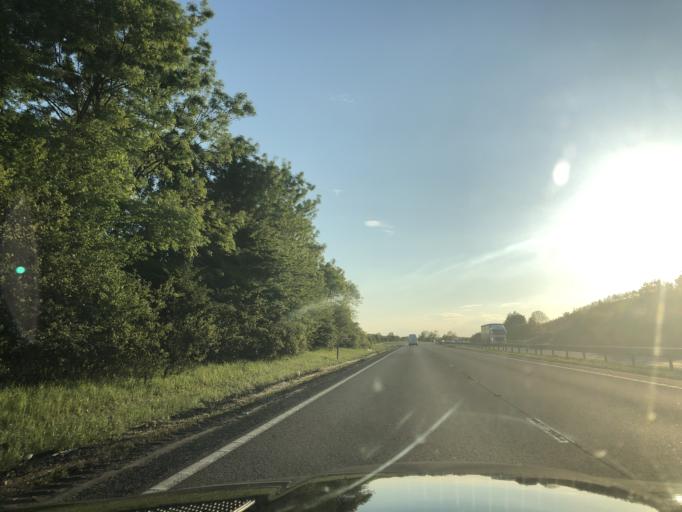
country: GB
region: England
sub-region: Northamptonshire
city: Thrapston
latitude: 52.3907
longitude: -0.5580
